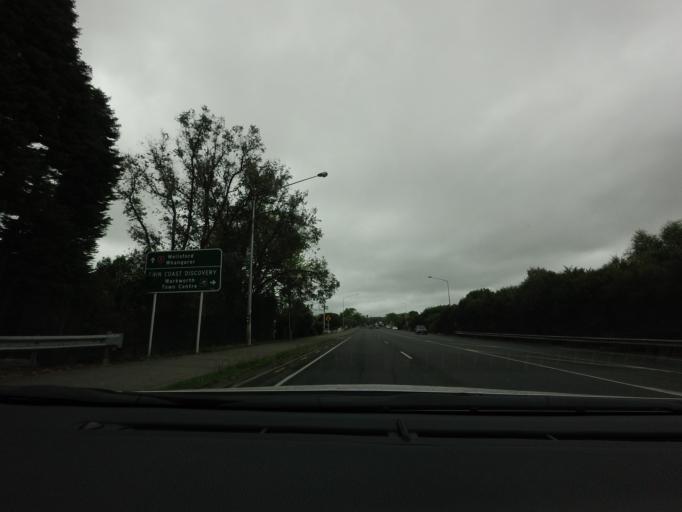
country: NZ
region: Auckland
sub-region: Auckland
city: Warkworth
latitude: -36.4041
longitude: 174.6580
